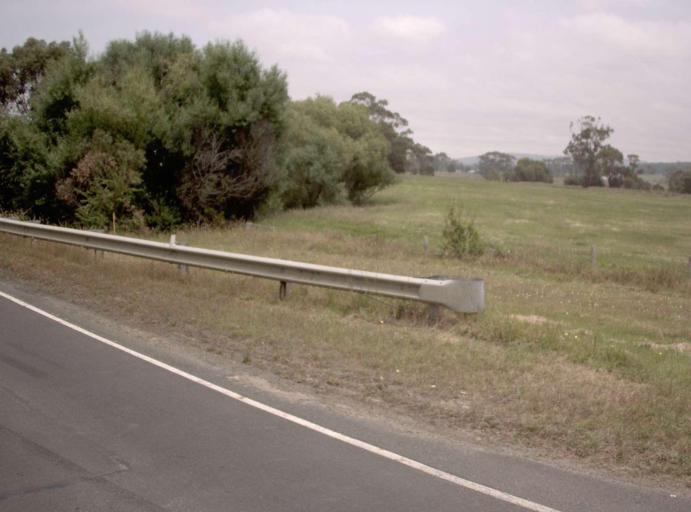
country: AU
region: Victoria
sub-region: Latrobe
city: Traralgon
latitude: -38.4660
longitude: 146.7185
